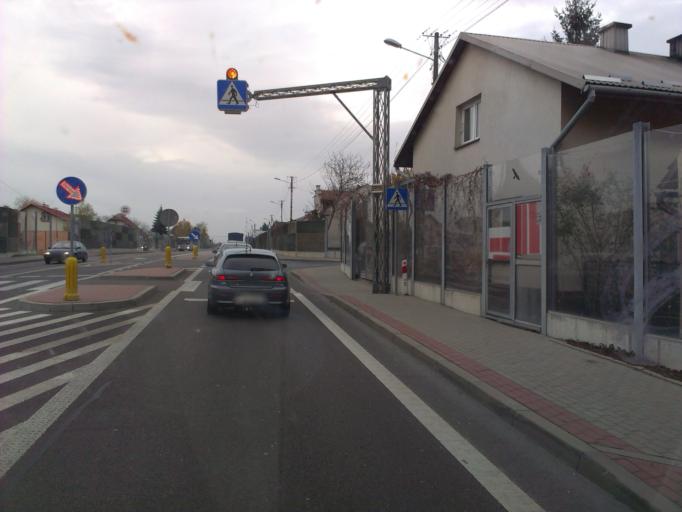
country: PL
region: Subcarpathian Voivodeship
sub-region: Powiat rzeszowski
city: Krasne
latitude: 50.0414
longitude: 22.0938
